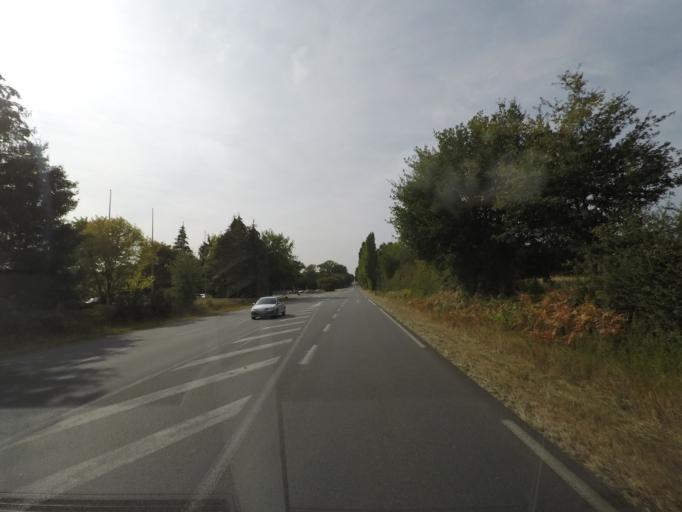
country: FR
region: Poitou-Charentes
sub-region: Departement des Deux-Sevres
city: Chef-Boutonne
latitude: 46.1813
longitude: -0.0270
